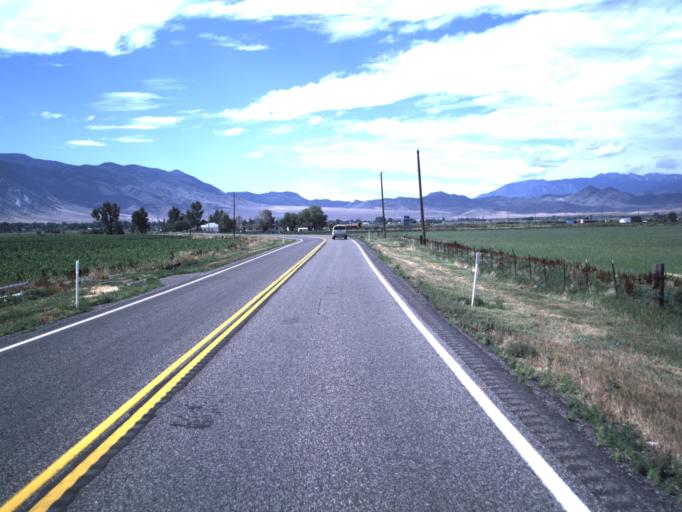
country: US
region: Utah
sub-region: Sevier County
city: Monroe
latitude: 38.6653
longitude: -112.1211
